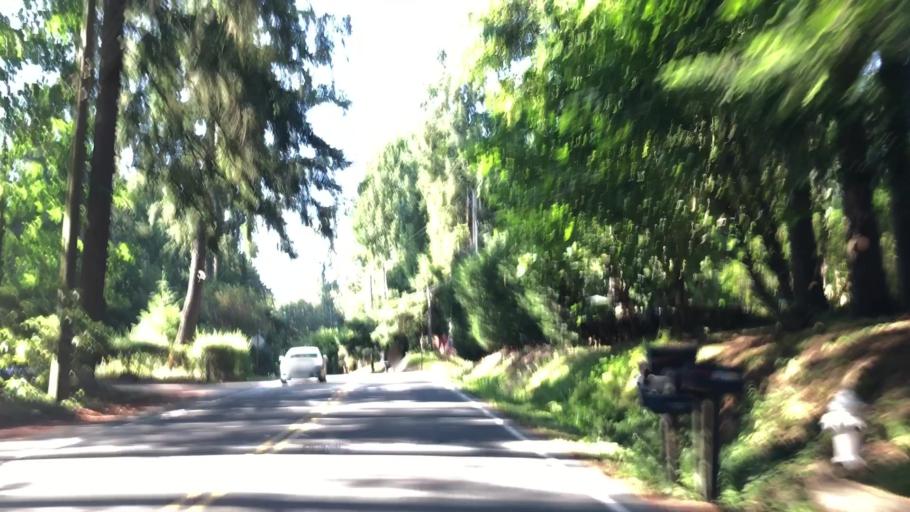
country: US
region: Washington
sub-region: King County
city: Lake Forest Park
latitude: 47.7703
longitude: -122.2856
